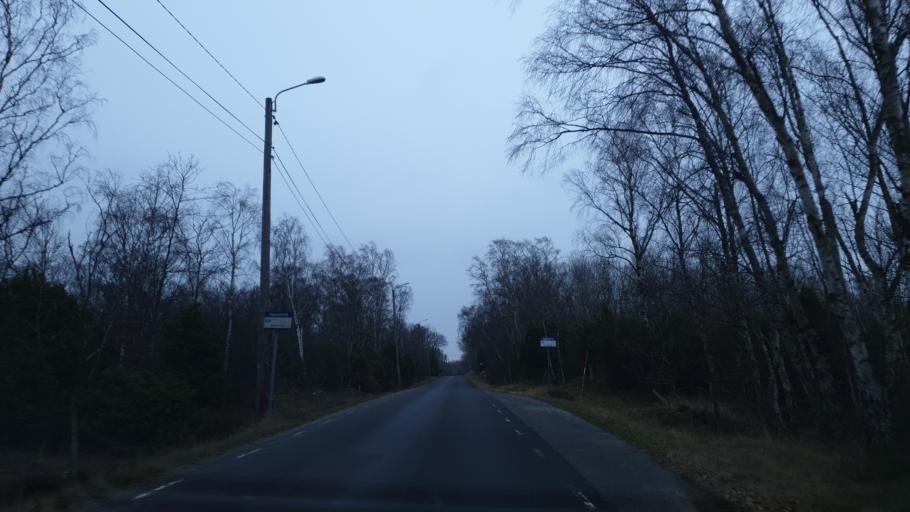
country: SE
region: Blekinge
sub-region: Karlskrona Kommun
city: Karlskrona
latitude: 56.1093
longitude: 15.6242
